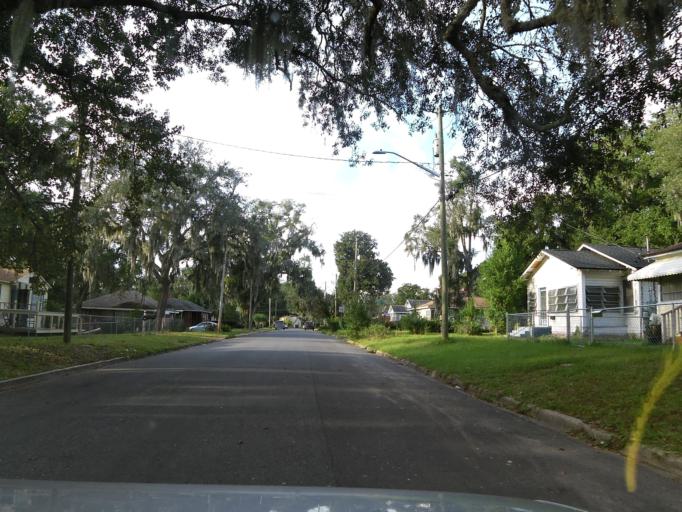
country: US
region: Florida
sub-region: Duval County
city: Jacksonville
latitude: 30.3855
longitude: -81.6619
